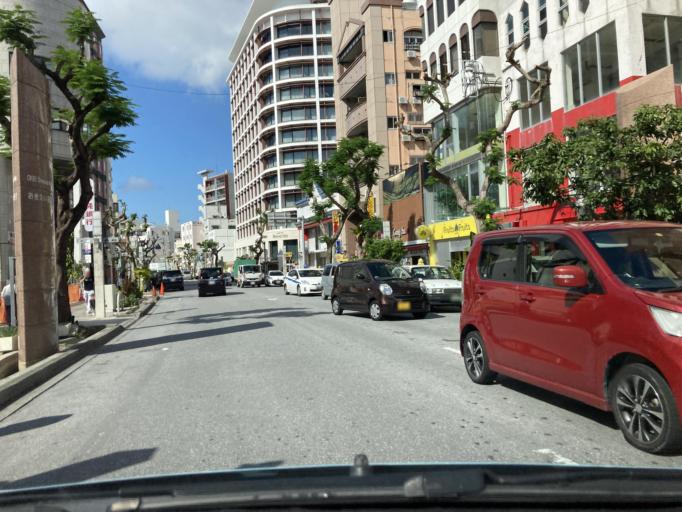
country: JP
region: Okinawa
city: Naha-shi
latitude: 26.2164
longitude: 127.6880
